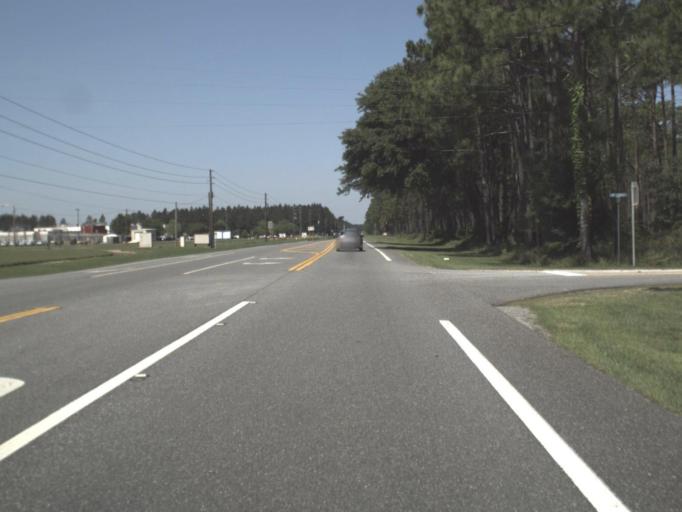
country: US
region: Florida
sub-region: Columbia County
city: Watertown
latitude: 30.1953
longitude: -82.5030
